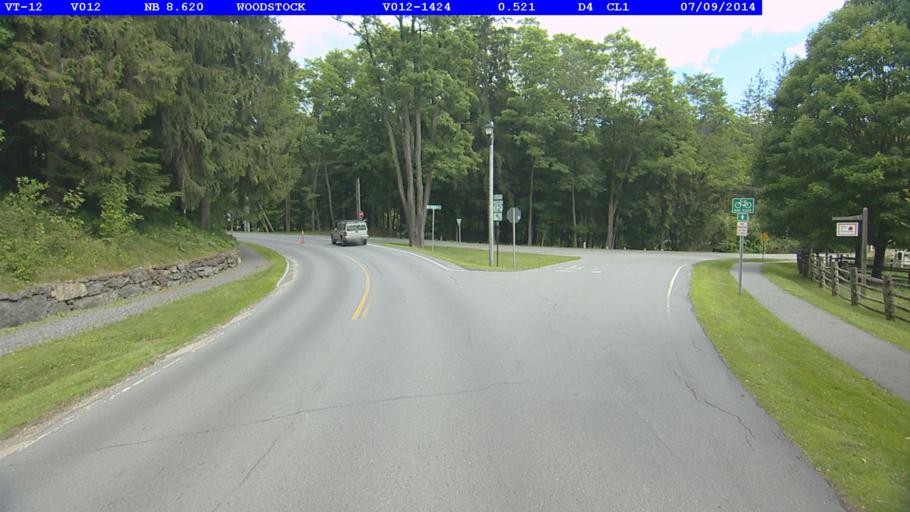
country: US
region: Vermont
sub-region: Windsor County
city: Woodstock
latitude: 43.6322
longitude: -72.5171
